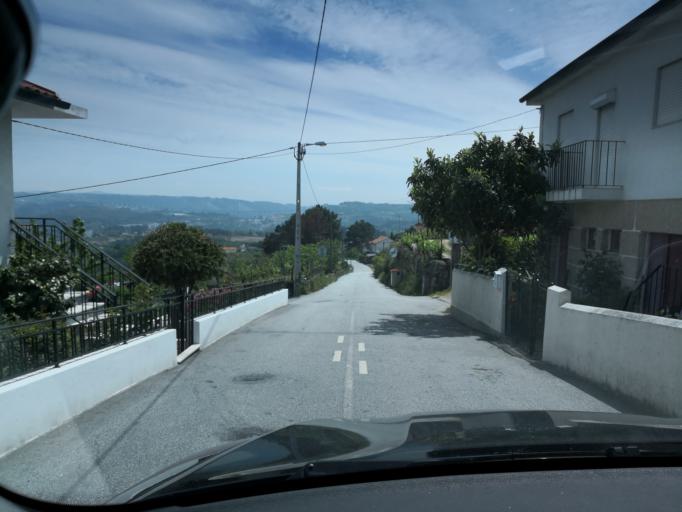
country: PT
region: Vila Real
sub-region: Vila Real
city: Vila Real
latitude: 41.3096
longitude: -7.7807
